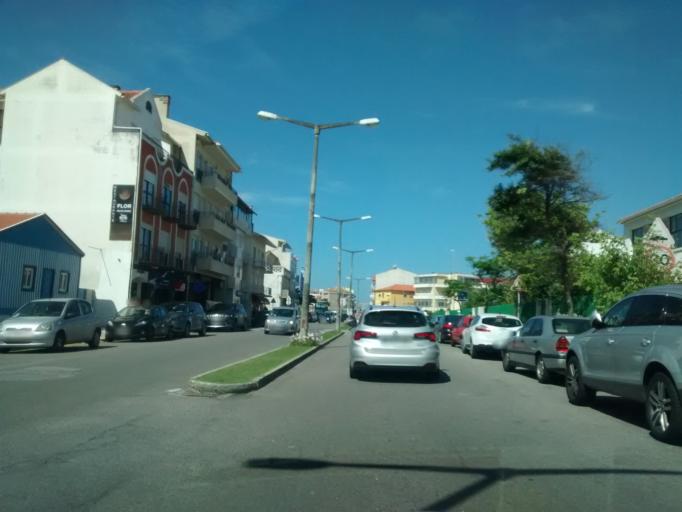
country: PT
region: Coimbra
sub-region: Mira
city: Mira
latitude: 40.4557
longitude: -8.7972
